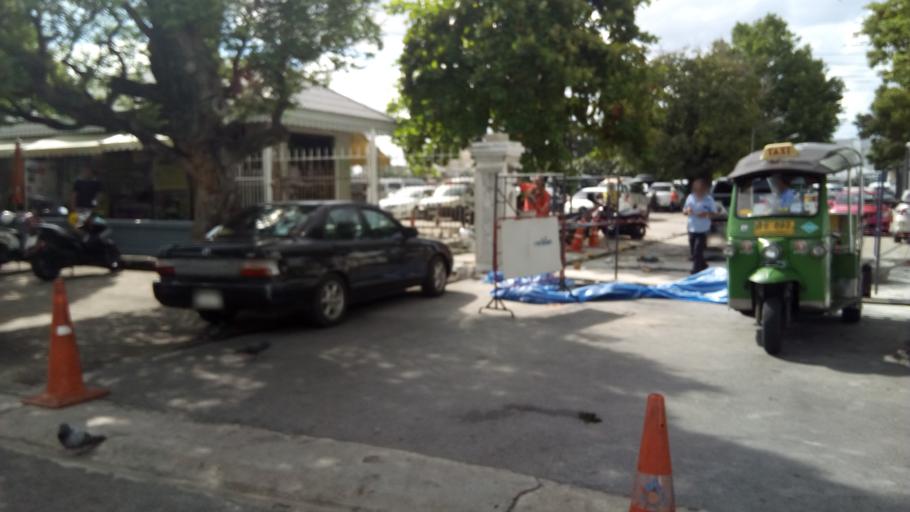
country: TH
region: Bangkok
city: Bangkok
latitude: 13.7503
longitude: 100.4895
